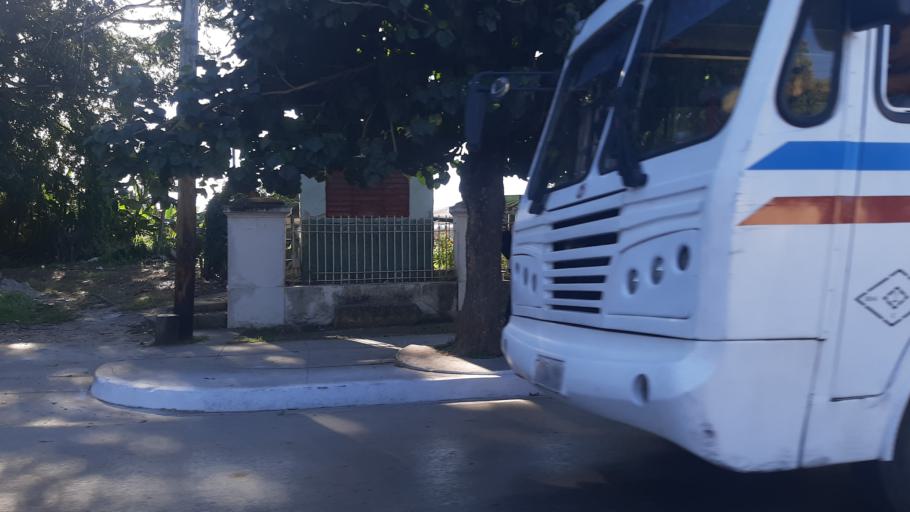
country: CU
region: Villa Clara
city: Santa Clara
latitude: 22.4110
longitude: -79.9590
